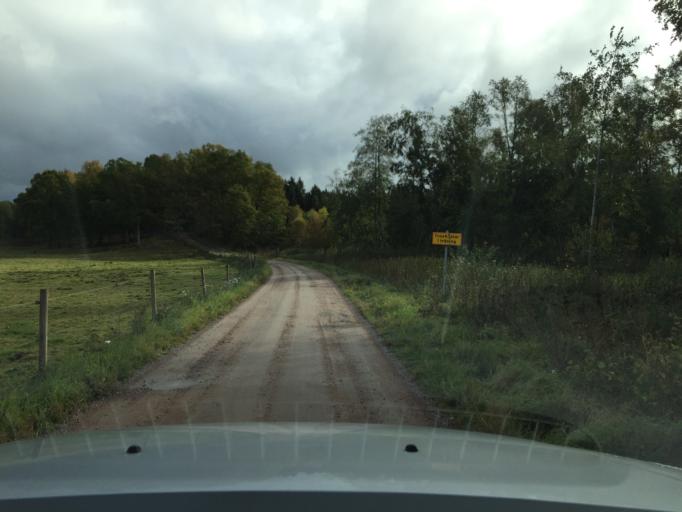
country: SE
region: Skane
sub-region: Hassleholms Kommun
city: Sosdala
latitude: 56.0526
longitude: 13.7236
